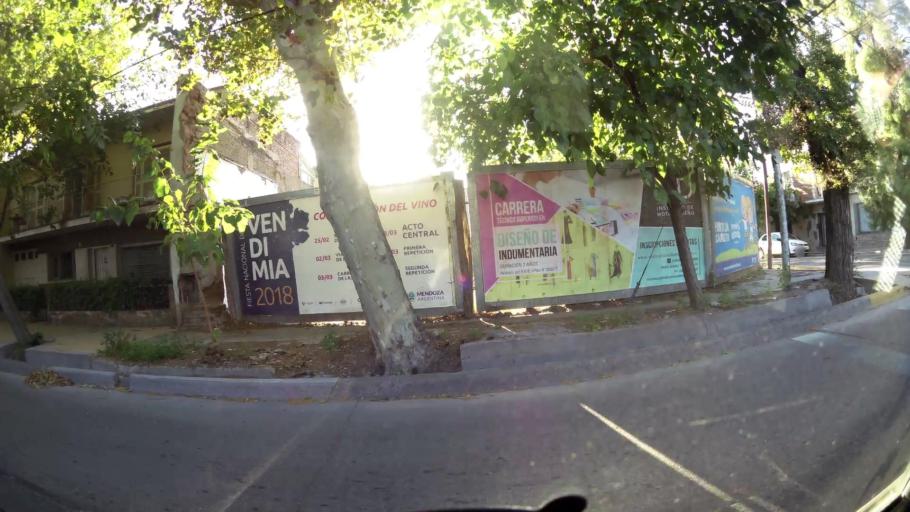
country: AR
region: Mendoza
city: Mendoza
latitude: -32.8740
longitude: -68.8293
